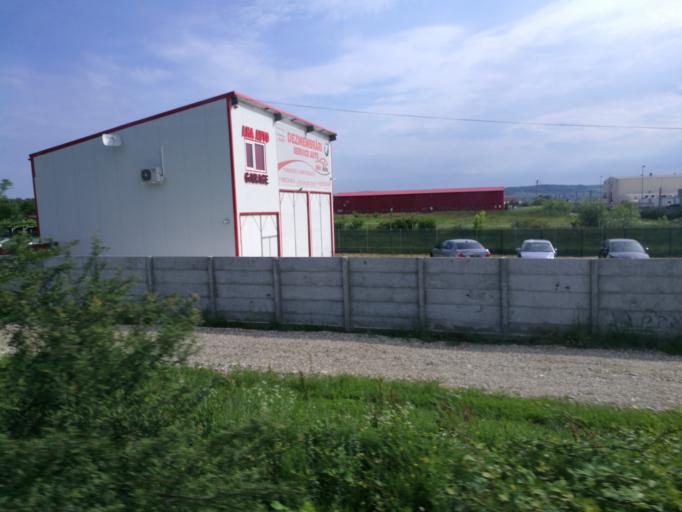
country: RO
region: Arges
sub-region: Comuna Bradu
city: Geamana
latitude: 44.8304
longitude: 24.9179
